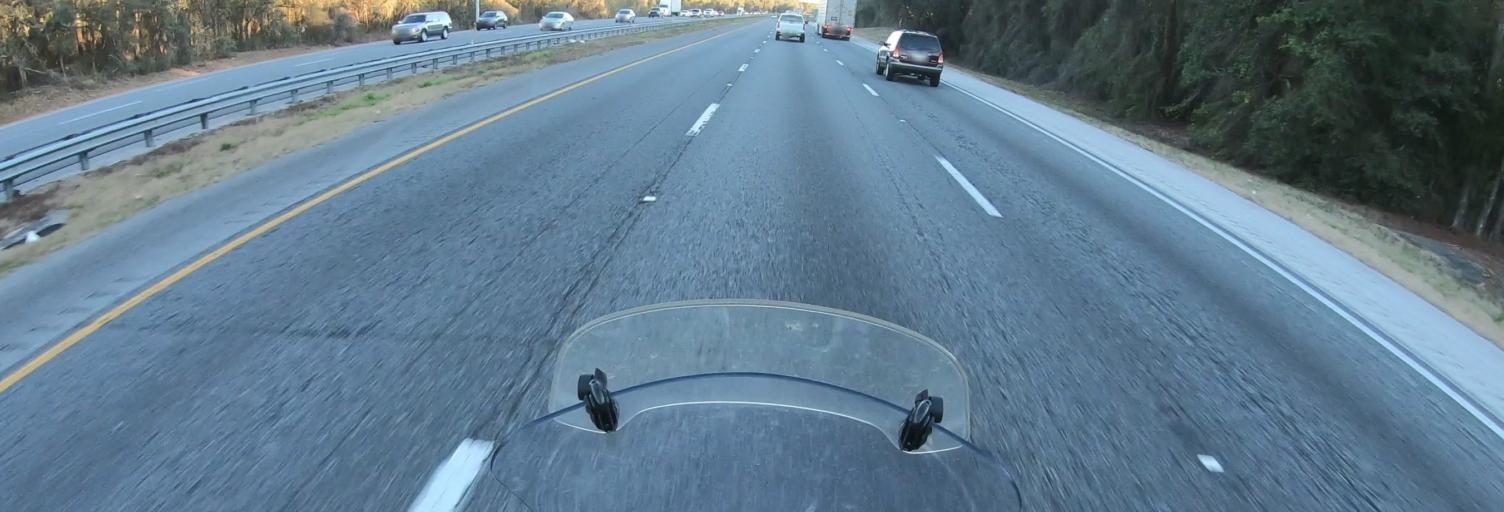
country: US
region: Florida
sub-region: Marion County
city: Belleview
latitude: 29.0474
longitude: -82.1666
